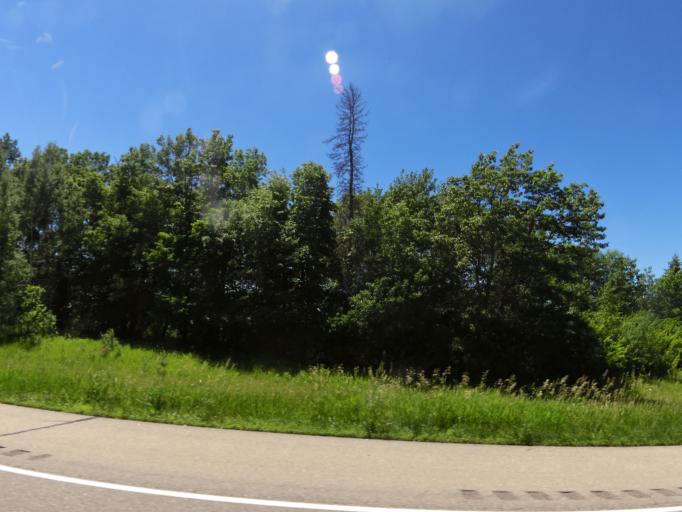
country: US
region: Minnesota
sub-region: Otter Tail County
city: New York Mills
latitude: 46.5186
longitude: -95.3584
